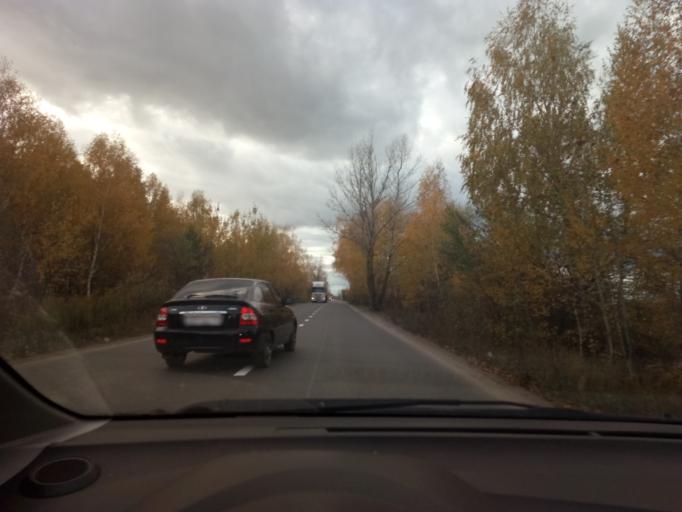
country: RU
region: Tatarstan
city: Staroye Arakchino
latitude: 55.8847
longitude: 48.9963
